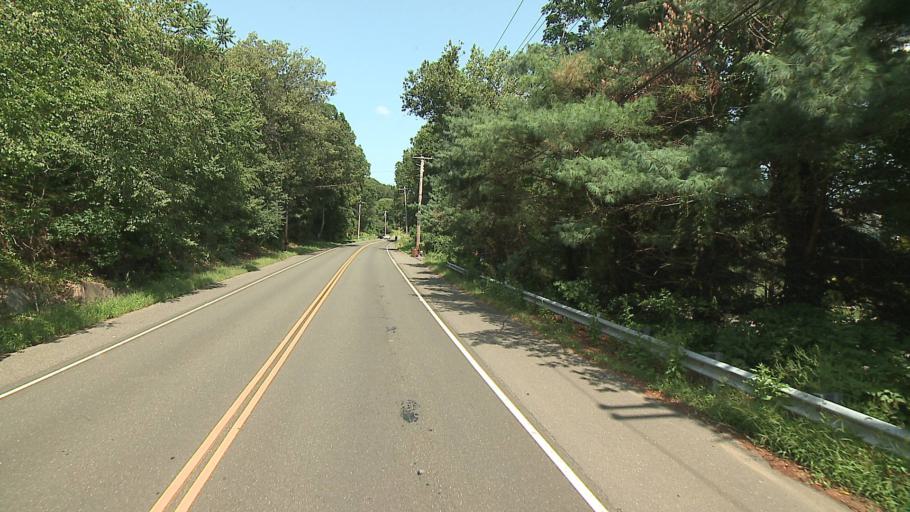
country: US
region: Connecticut
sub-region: Fairfield County
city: Shelton
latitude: 41.2836
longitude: -73.0848
